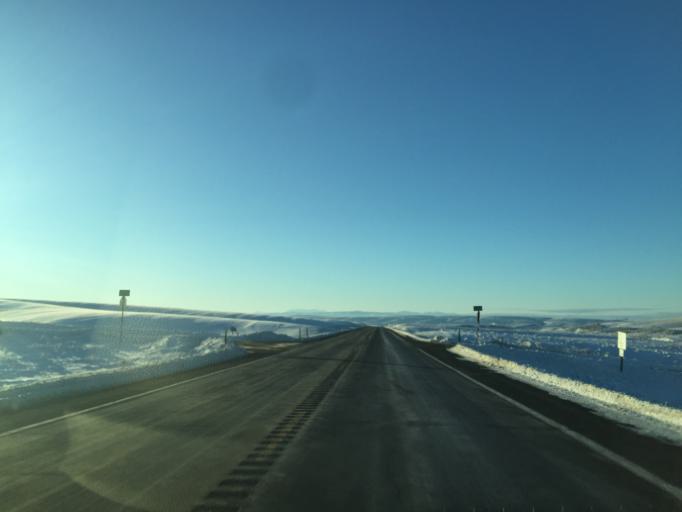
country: US
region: Washington
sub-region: Grant County
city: Soap Lake
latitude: 47.5994
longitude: -119.5975
